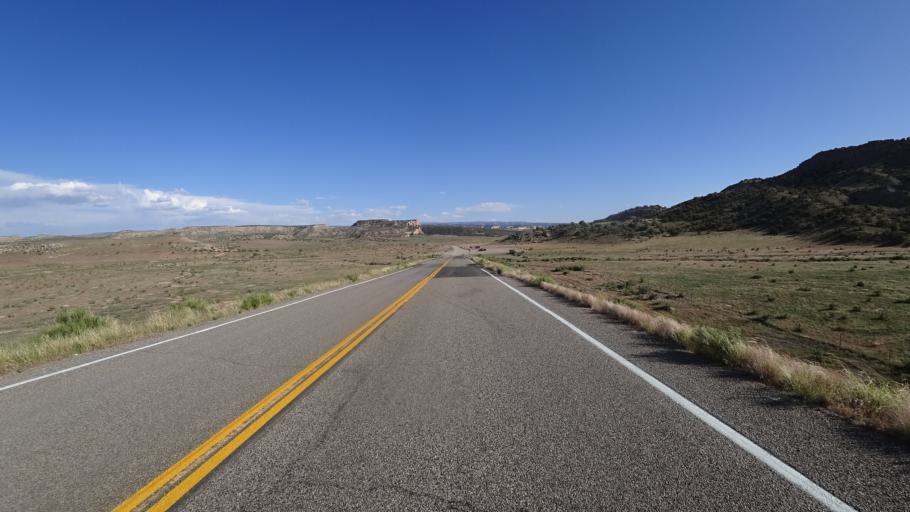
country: US
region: Colorado
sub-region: Mesa County
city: Loma
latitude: 39.1893
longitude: -109.0193
